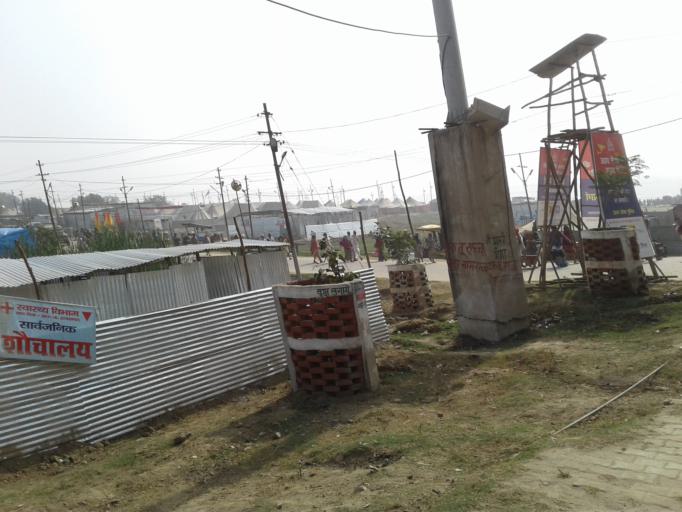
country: IN
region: Uttar Pradesh
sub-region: Allahabad
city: Jhusi
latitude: 25.4306
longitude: 81.8785
